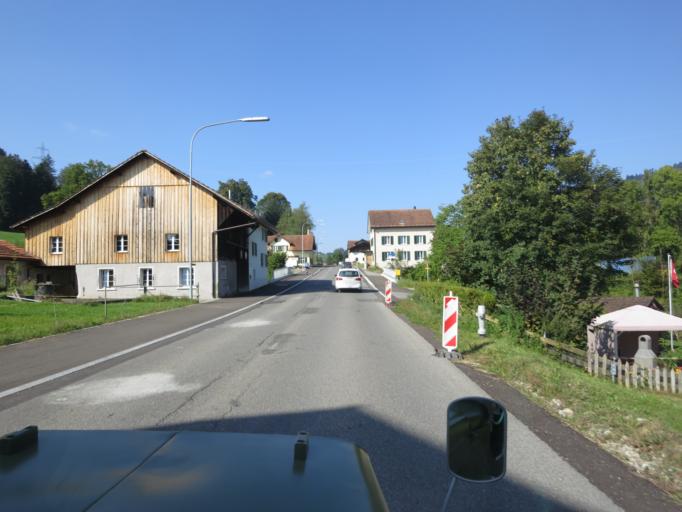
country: CH
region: Zurich
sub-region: Bezirk Hinwil
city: Wald
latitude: 47.2932
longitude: 8.9165
